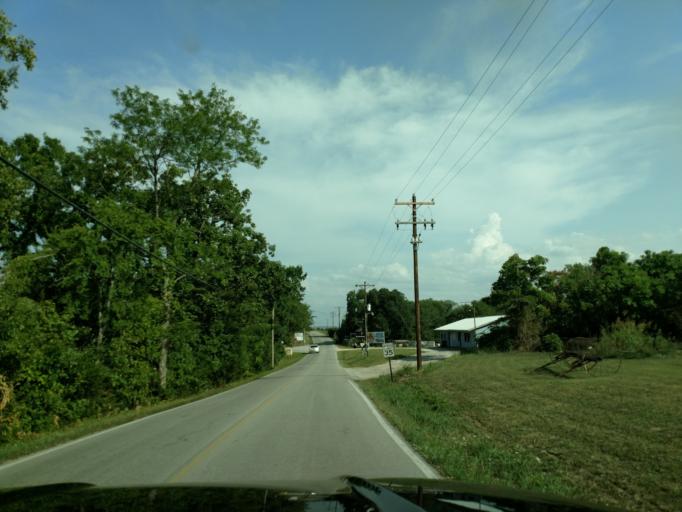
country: US
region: Missouri
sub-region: Barry County
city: Shell Knob
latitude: 36.6102
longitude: -93.5716
